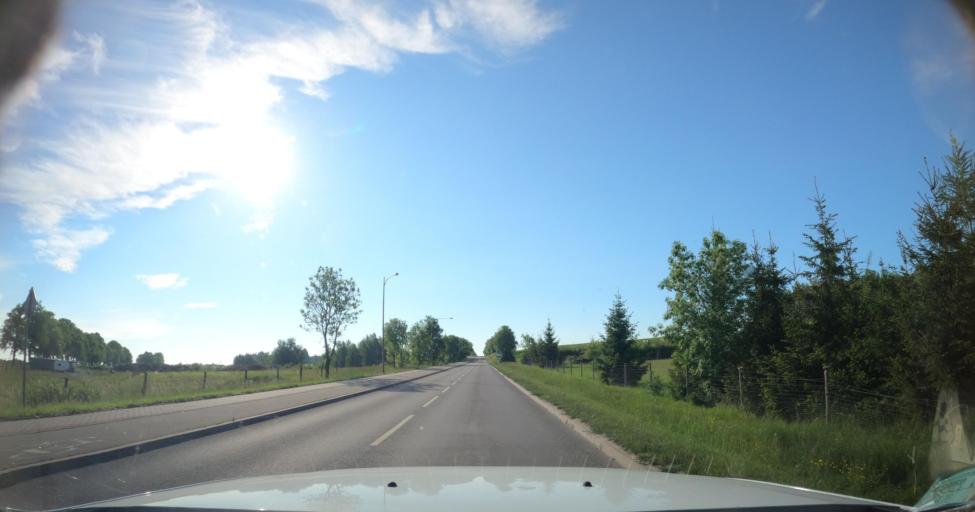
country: PL
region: Warmian-Masurian Voivodeship
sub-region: Powiat elblaski
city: Paslek
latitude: 54.0743
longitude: 19.6382
